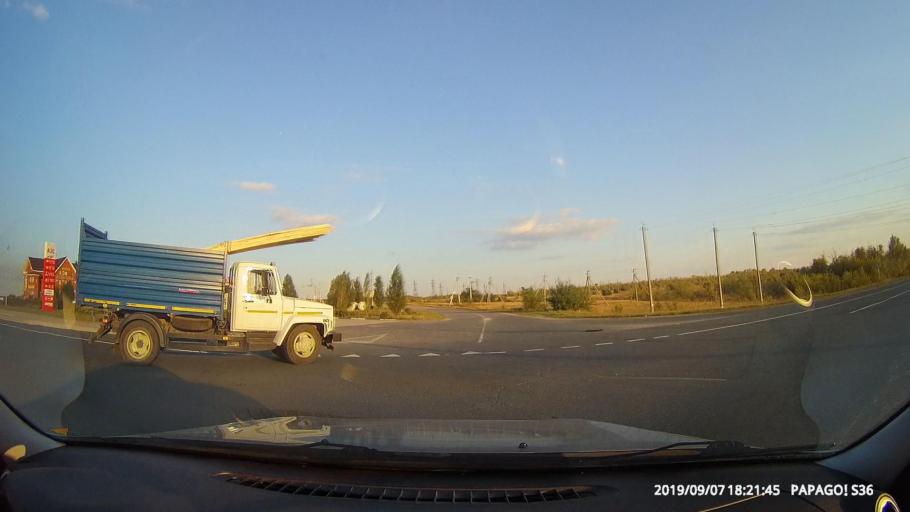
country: RU
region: Samara
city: Chapayevsk
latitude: 52.9920
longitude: 49.7763
